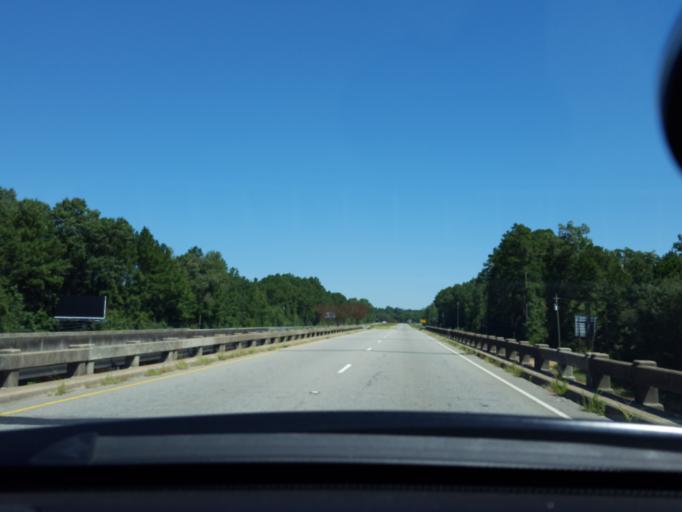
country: US
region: North Carolina
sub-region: Bladen County
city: Elizabethtown
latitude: 34.6374
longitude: -78.5989
